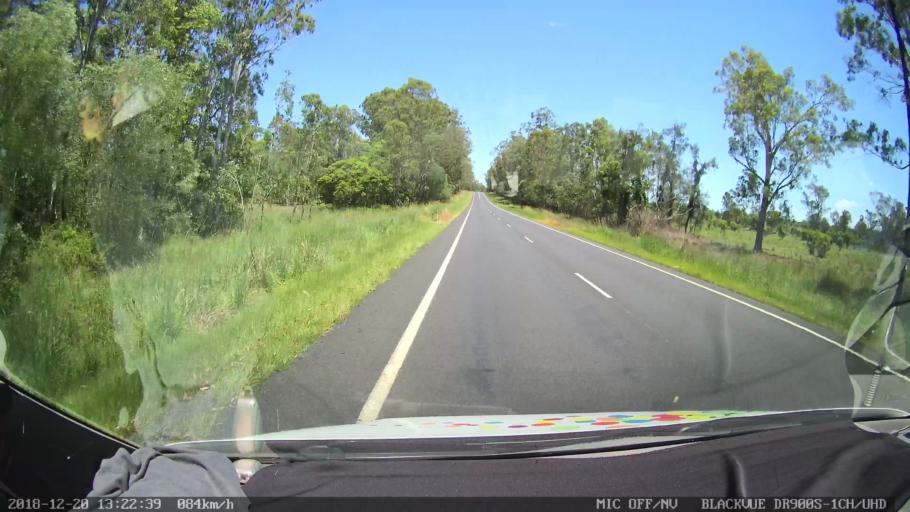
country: AU
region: New South Wales
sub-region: Richmond Valley
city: Casino
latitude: -29.0942
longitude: 153.0013
